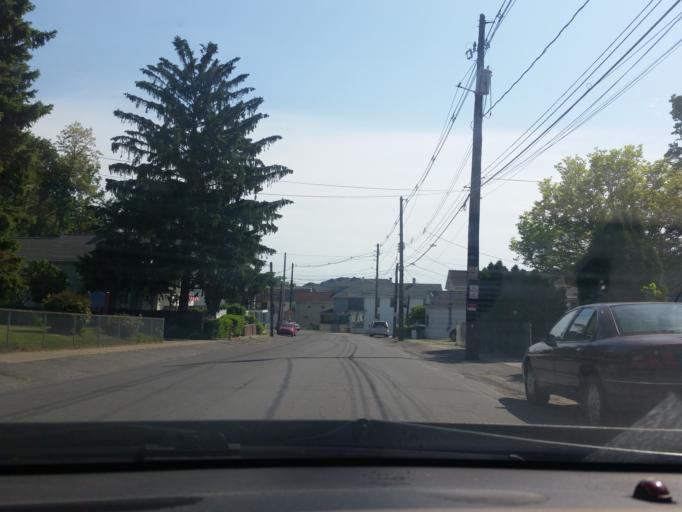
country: US
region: Pennsylvania
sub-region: Luzerne County
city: Luzerne
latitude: 41.2869
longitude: -75.8954
